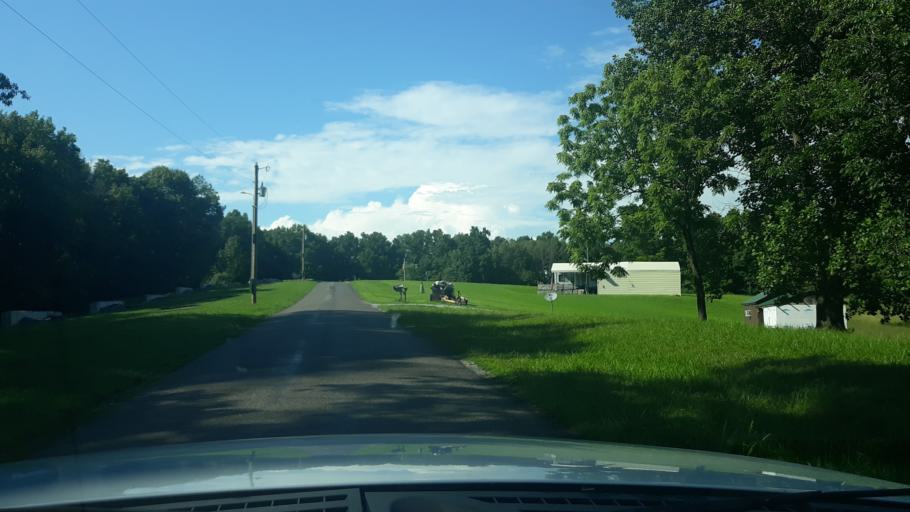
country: US
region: Illinois
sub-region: Saline County
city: Harrisburg
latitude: 37.8541
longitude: -88.5856
